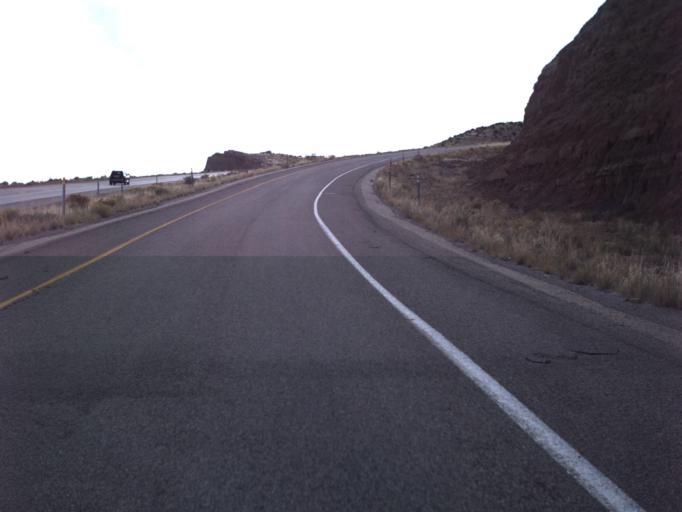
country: US
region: Utah
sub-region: Emery County
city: Ferron
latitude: 38.8355
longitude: -111.1058
